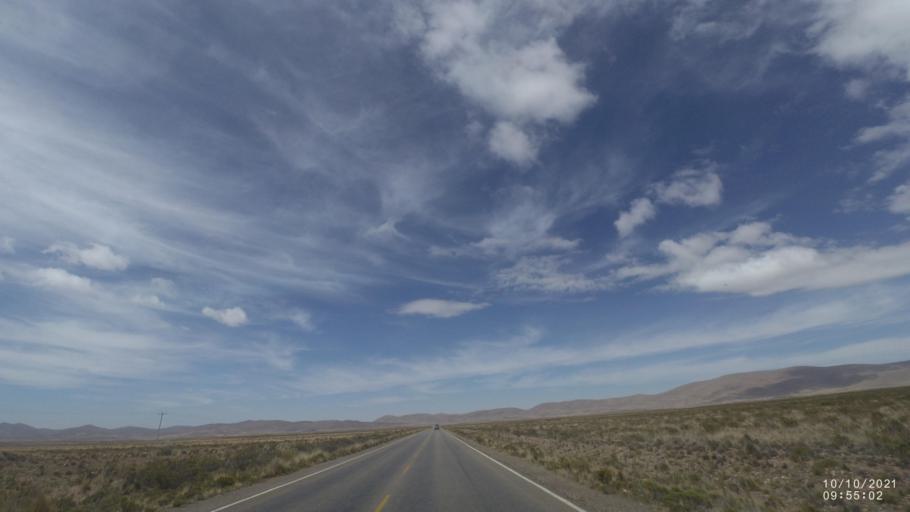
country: BO
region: La Paz
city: Colquiri
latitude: -17.3015
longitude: -67.3629
